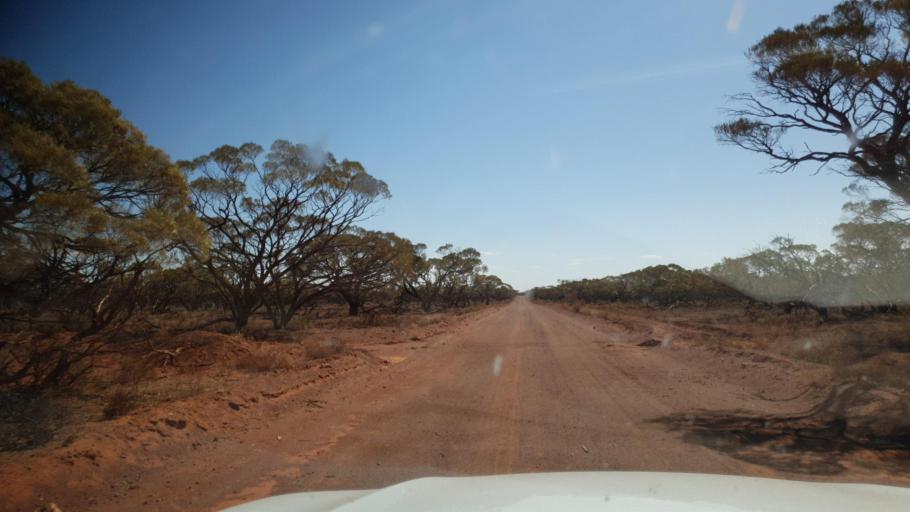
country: AU
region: South Australia
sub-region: Kimba
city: Caralue
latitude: -32.5260
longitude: 136.1668
